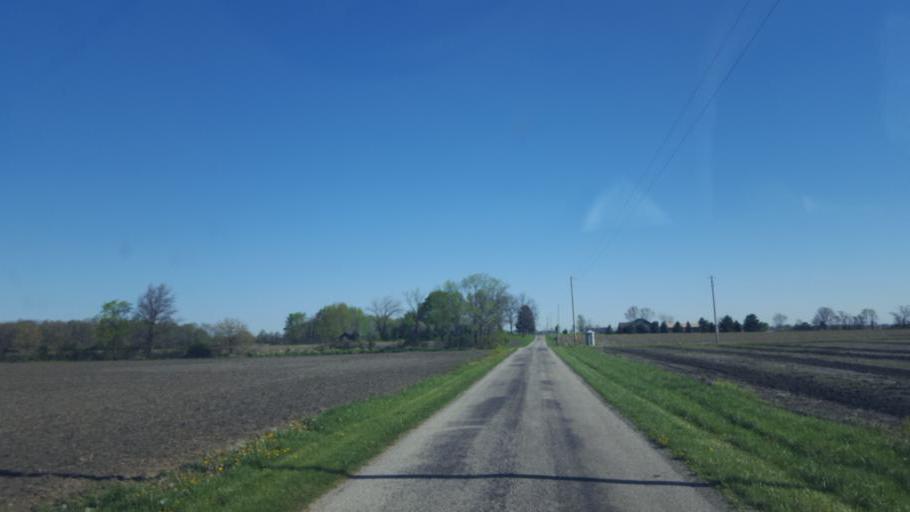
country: US
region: Ohio
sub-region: Crawford County
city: Bucyrus
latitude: 40.6622
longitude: -82.9817
